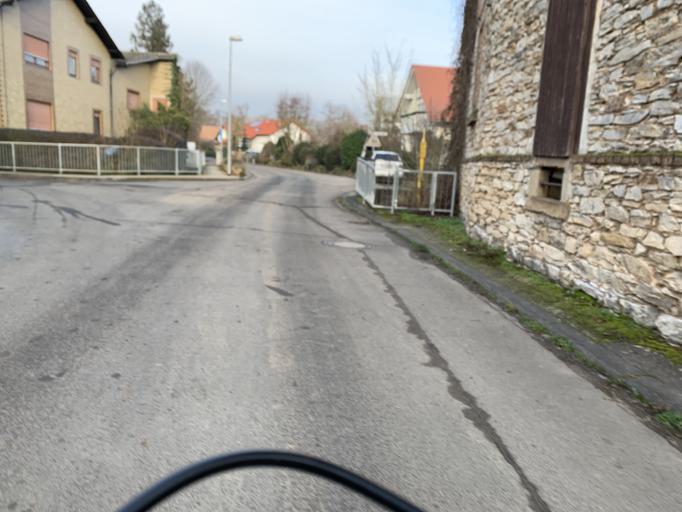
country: DE
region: Rheinland-Pfalz
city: Windesheim
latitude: 49.9061
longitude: 7.8146
